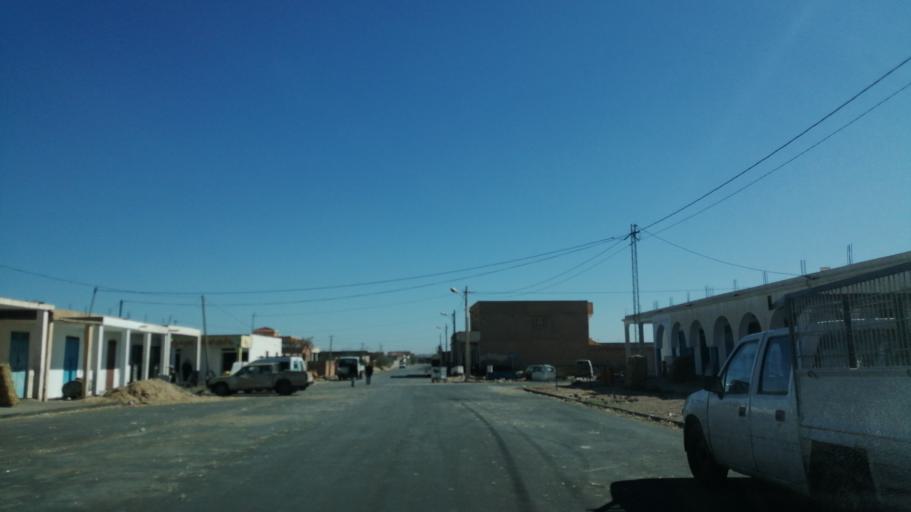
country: TN
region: Sidi Bu Zayd
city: Bi'r al Hufayy
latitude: 34.8520
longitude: 9.1457
